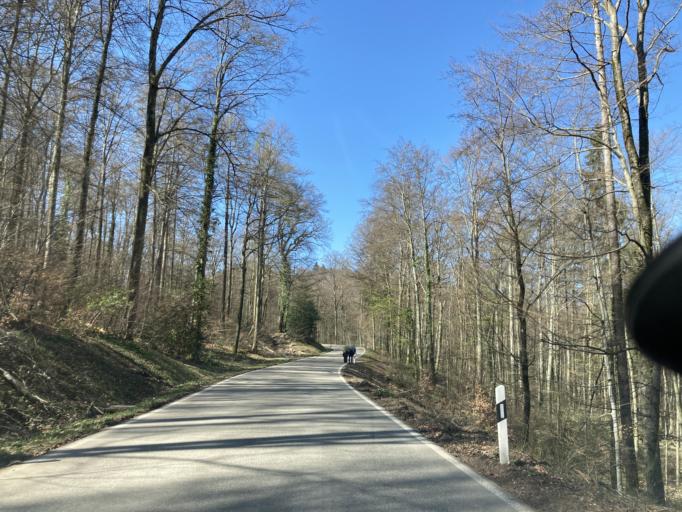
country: DE
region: Baden-Wuerttemberg
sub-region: Freiburg Region
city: Badenweiler
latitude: 47.7781
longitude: 7.6704
